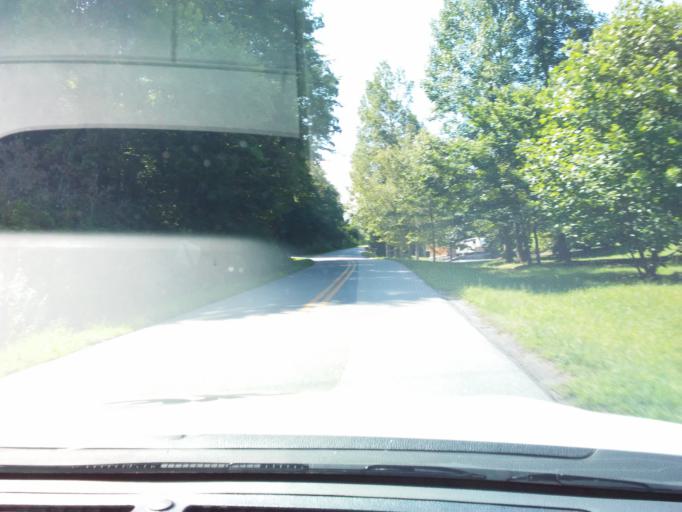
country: US
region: Georgia
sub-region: Union County
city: Blairsville
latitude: 34.9311
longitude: -83.8667
